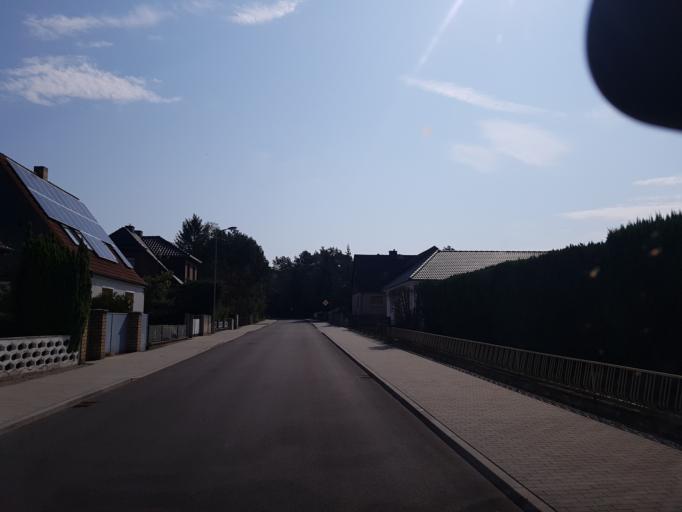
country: DE
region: Brandenburg
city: Lauchhammer
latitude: 51.5123
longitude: 13.7171
